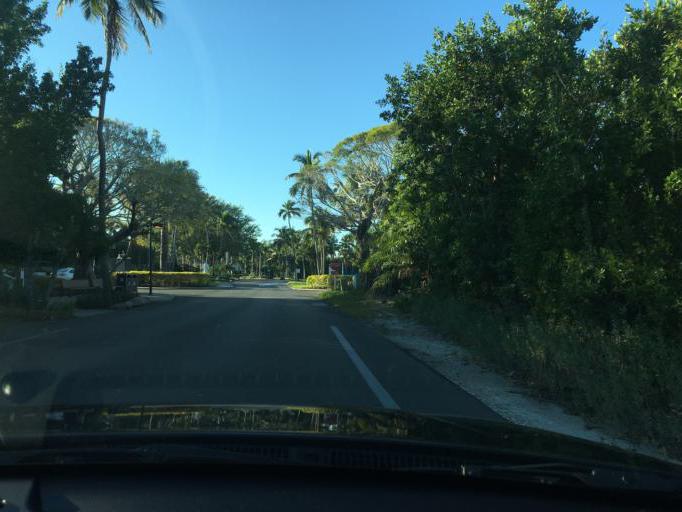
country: US
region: Florida
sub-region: Lee County
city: Pine Island Center
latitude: 26.5284
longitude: -82.1920
